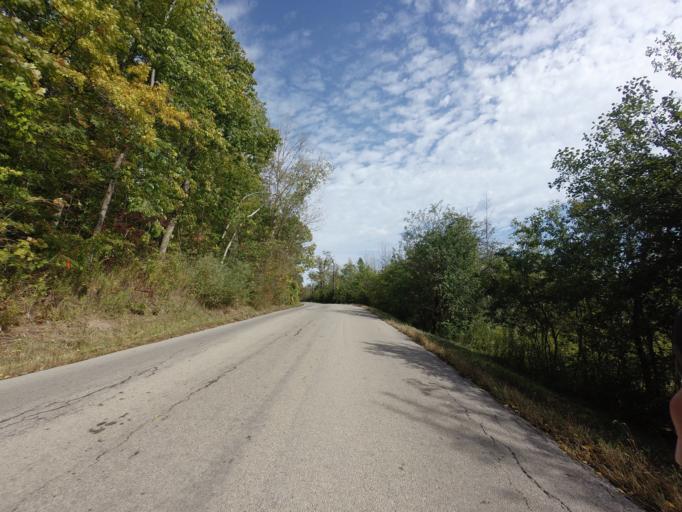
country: CA
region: Ontario
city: Hamilton
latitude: 43.2990
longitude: -79.9243
